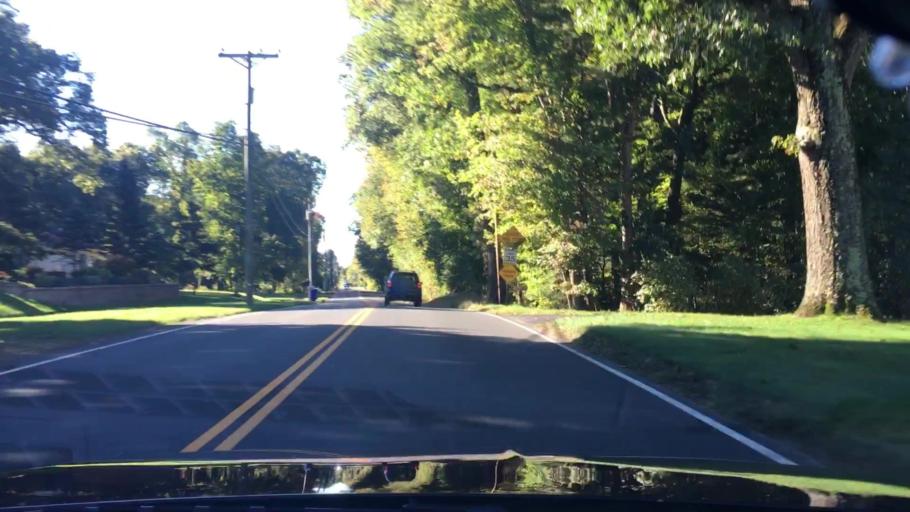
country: US
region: Connecticut
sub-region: Hartford County
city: Sherwood Manor
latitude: 42.0111
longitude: -72.5594
